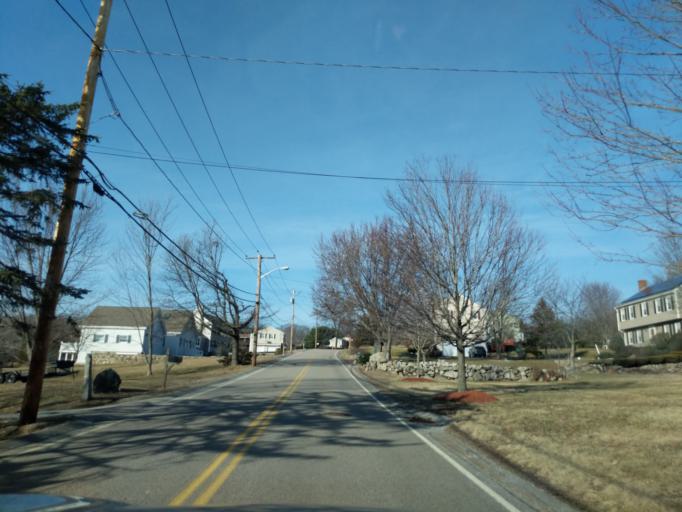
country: US
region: Massachusetts
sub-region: Worcester County
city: Blackstone
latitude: 42.0423
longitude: -71.5134
